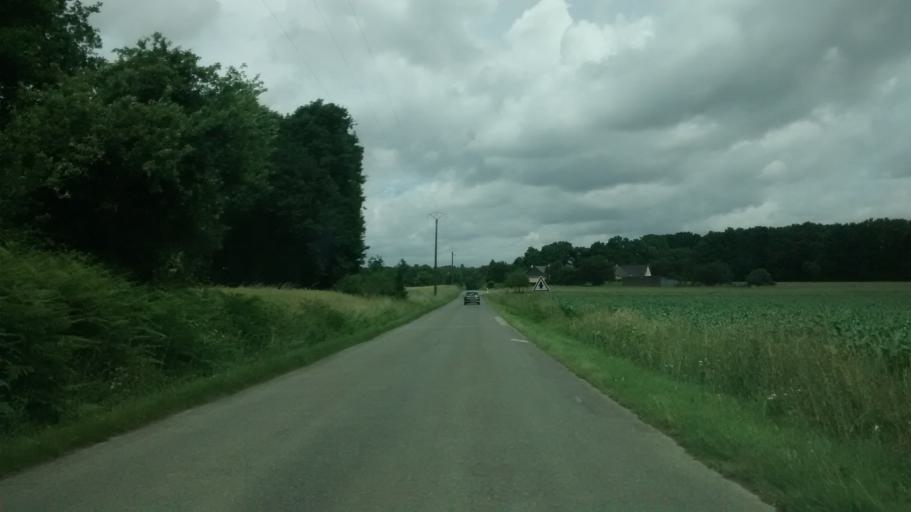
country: FR
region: Brittany
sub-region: Departement du Morbihan
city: La Gacilly
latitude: 47.7767
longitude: -2.1165
